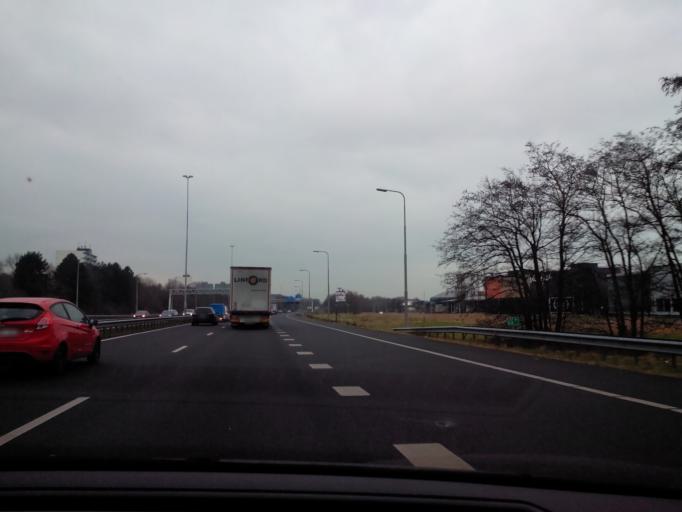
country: NL
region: North Brabant
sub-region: Gemeente Breda
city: Hoge Vucht
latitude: 51.5846
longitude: 4.8245
